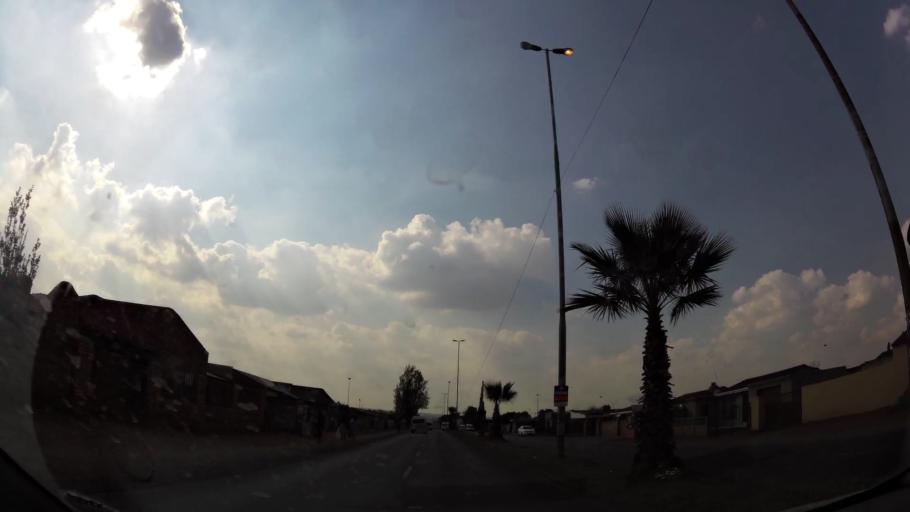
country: ZA
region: Gauteng
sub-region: Ekurhuleni Metropolitan Municipality
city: Germiston
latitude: -26.3168
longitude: 28.1508
